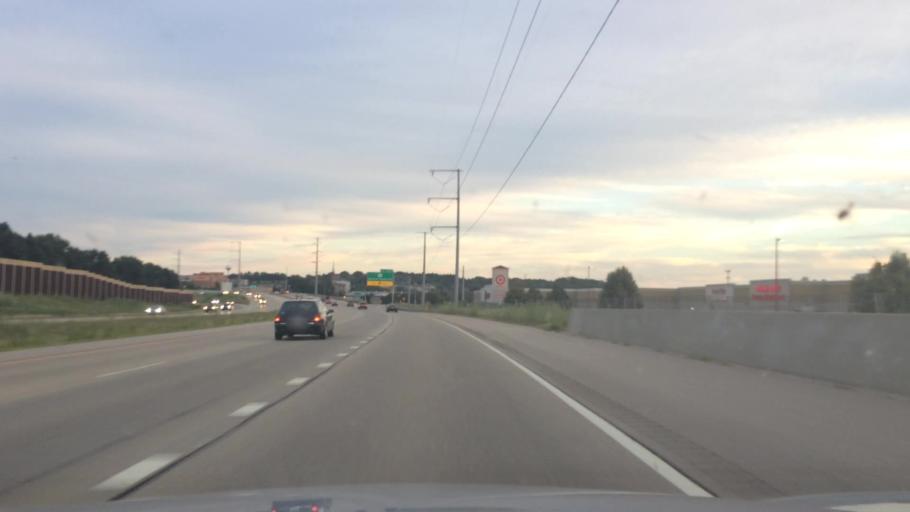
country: US
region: Wisconsin
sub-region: Dane County
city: Middleton
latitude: 43.0649
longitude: -89.5233
